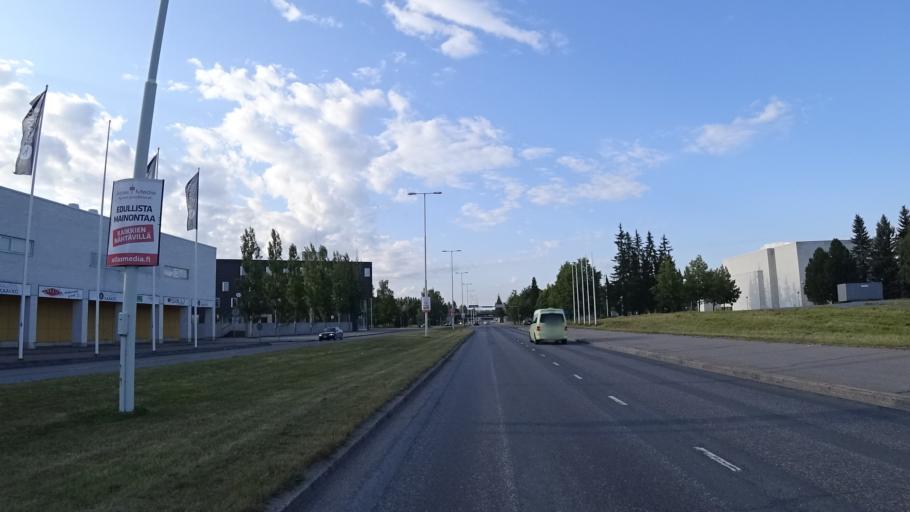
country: FI
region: South Karelia
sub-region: Imatra
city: Imatra
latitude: 61.1904
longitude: 28.7771
